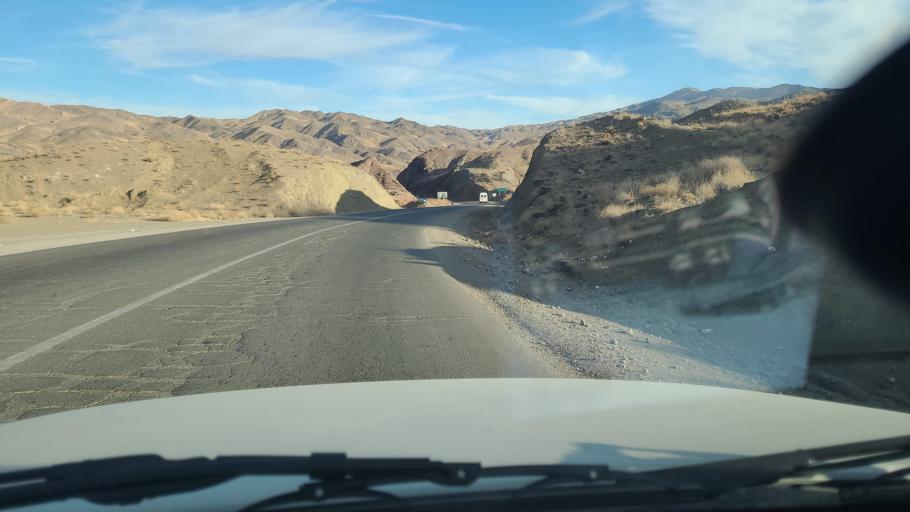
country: IR
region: Razavi Khorasan
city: Sabzevar
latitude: 36.4192
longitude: 57.5585
